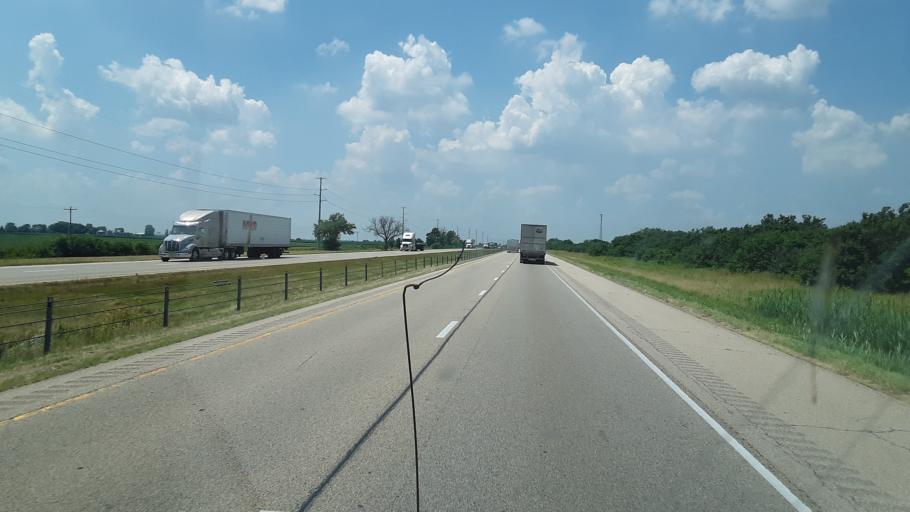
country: US
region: Illinois
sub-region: LaSalle County
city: Ottawa
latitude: 41.3687
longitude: -88.8978
